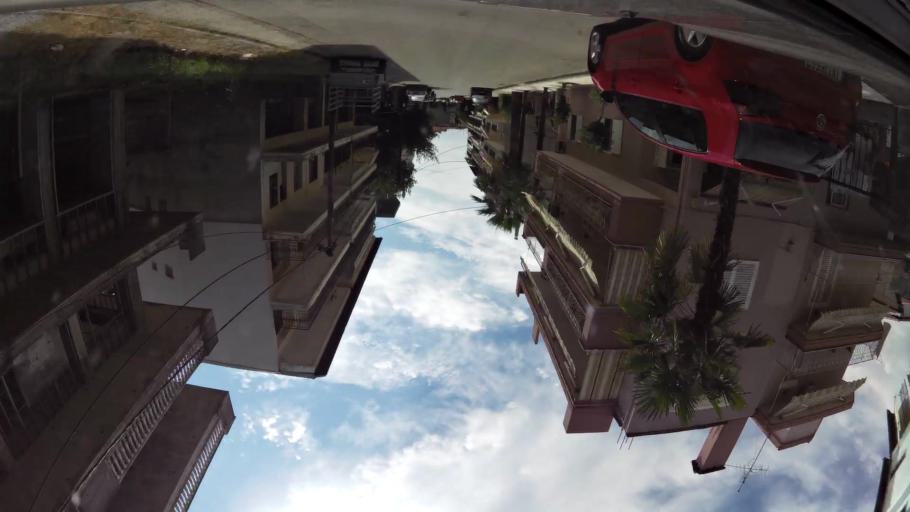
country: GR
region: Central Macedonia
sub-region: Nomos Pierias
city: Katerini
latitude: 40.2731
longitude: 22.4980
